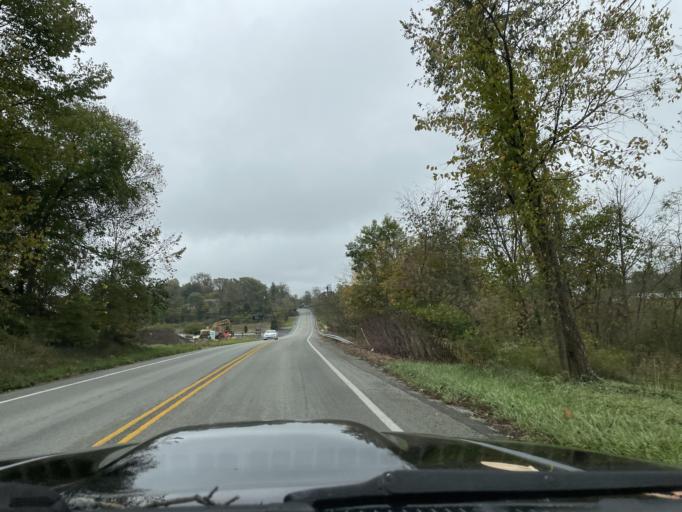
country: US
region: Pennsylvania
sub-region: Allegheny County
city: Springdale
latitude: 40.5300
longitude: -79.7849
